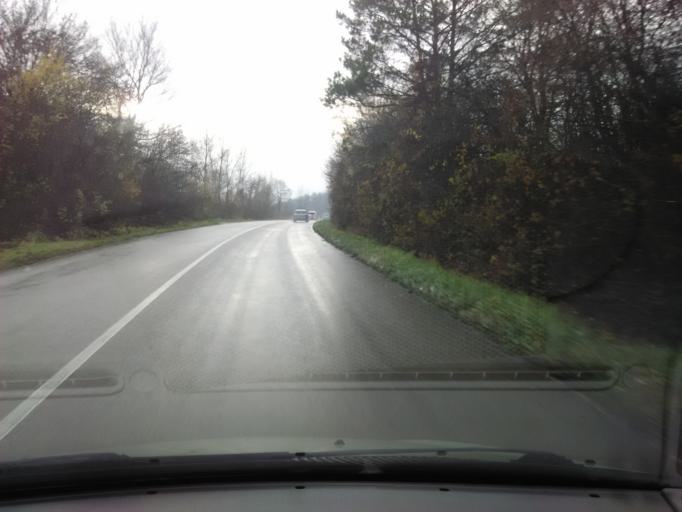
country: SK
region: Zilinsky
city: Bytca
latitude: 49.2055
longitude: 18.5179
